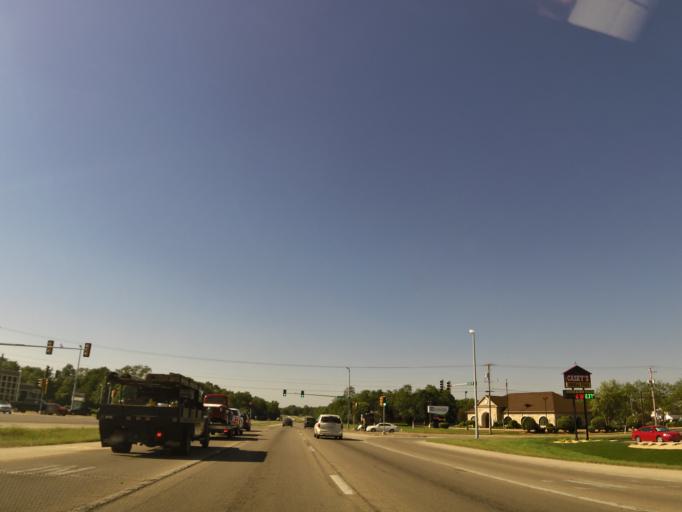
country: US
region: Illinois
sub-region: Winnebago County
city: Roscoe
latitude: 42.4122
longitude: -89.0128
